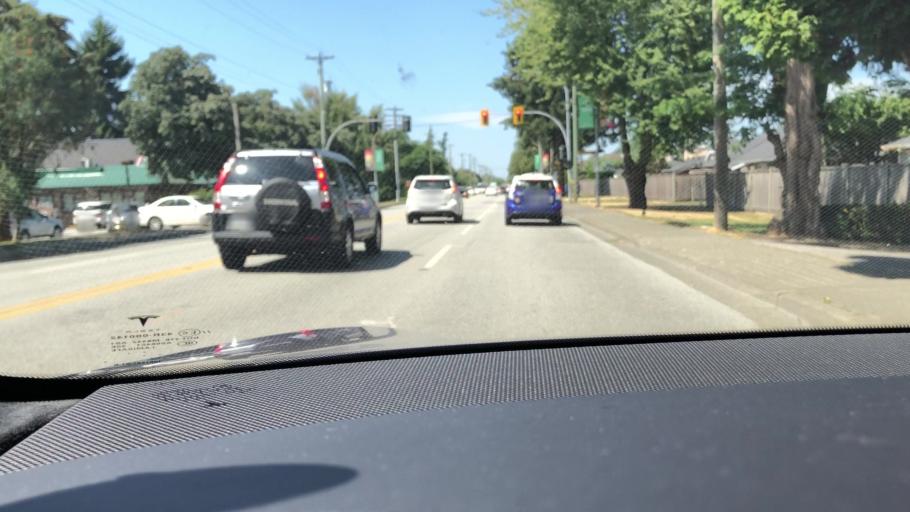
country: CA
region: British Columbia
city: Richmond
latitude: 49.1846
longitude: -123.0856
